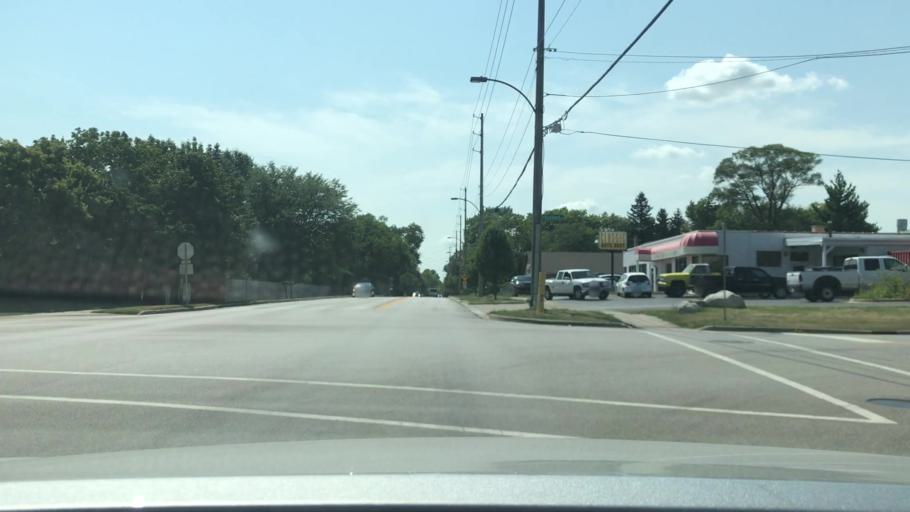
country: US
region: Illinois
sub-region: Kane County
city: Batavia
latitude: 41.8518
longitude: -88.2904
